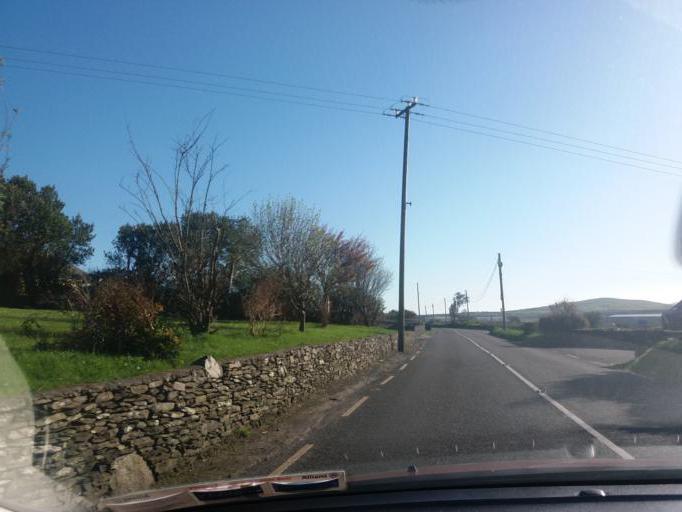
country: IE
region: Munster
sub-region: Ciarrai
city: Dingle
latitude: 52.1547
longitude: -10.2880
